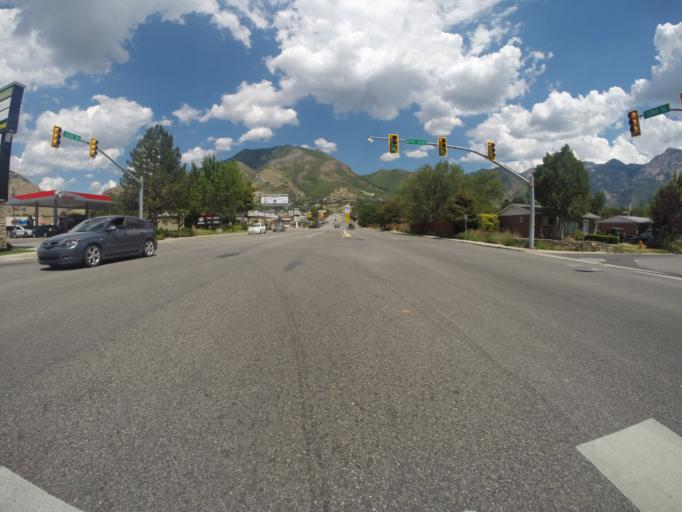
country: US
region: Utah
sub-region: Salt Lake County
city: East Millcreek
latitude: 40.6999
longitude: -111.8038
